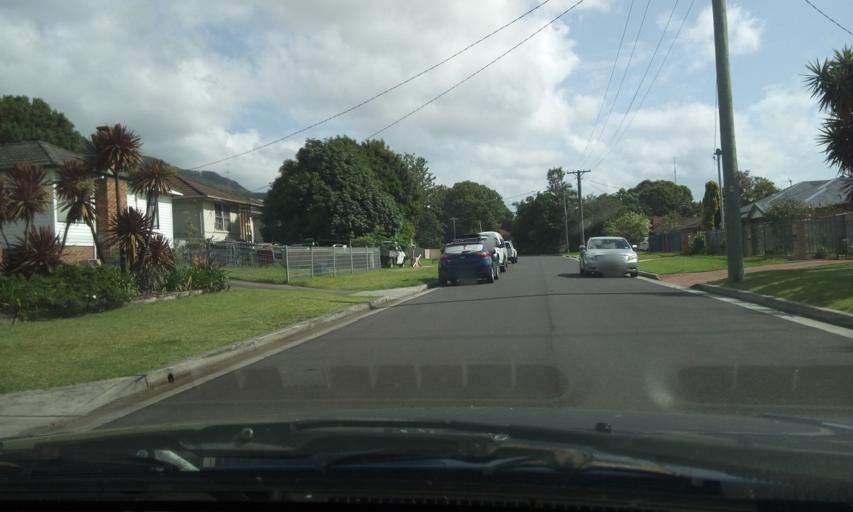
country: AU
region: New South Wales
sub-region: Wollongong
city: Corrimal
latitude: -34.3771
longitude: 150.8902
